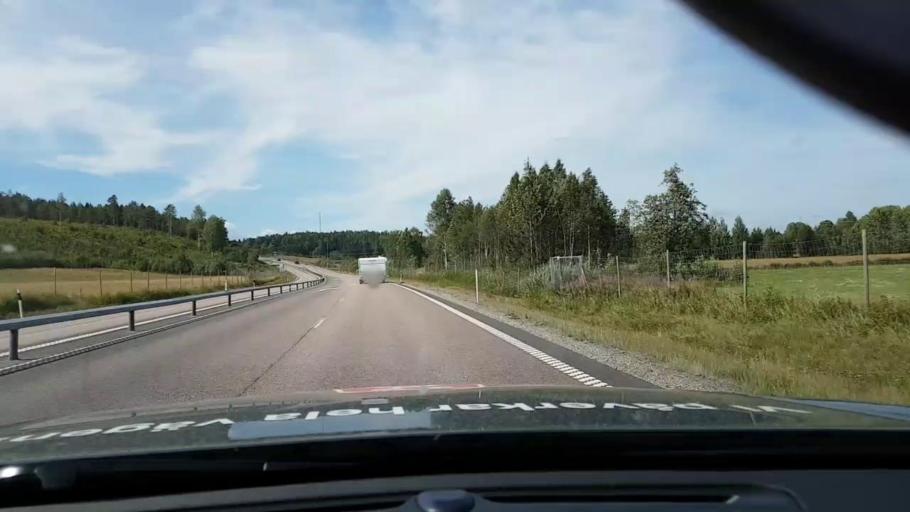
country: SE
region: Vaesternorrland
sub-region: OErnskoeldsviks Kommun
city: Ornskoldsvik
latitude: 63.3079
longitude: 18.8454
